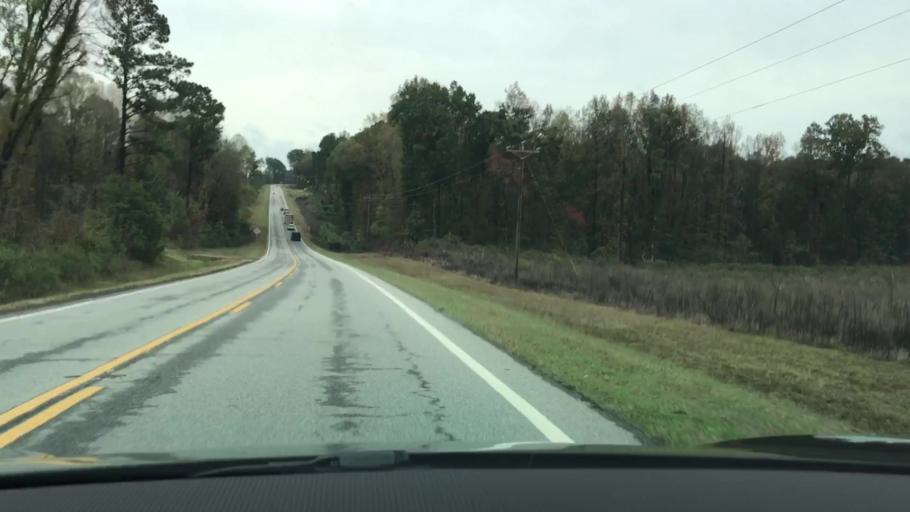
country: US
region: Georgia
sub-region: Greene County
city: Greensboro
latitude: 33.6114
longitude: -83.2069
